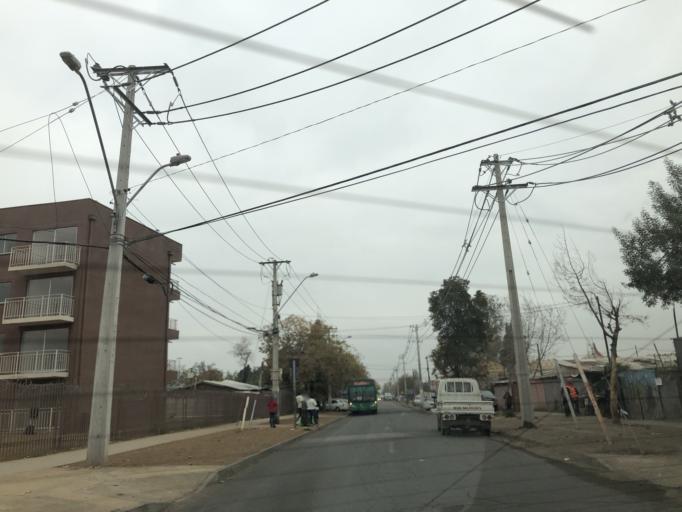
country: CL
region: Santiago Metropolitan
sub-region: Provincia de Santiago
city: La Pintana
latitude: -33.5803
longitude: -70.6063
